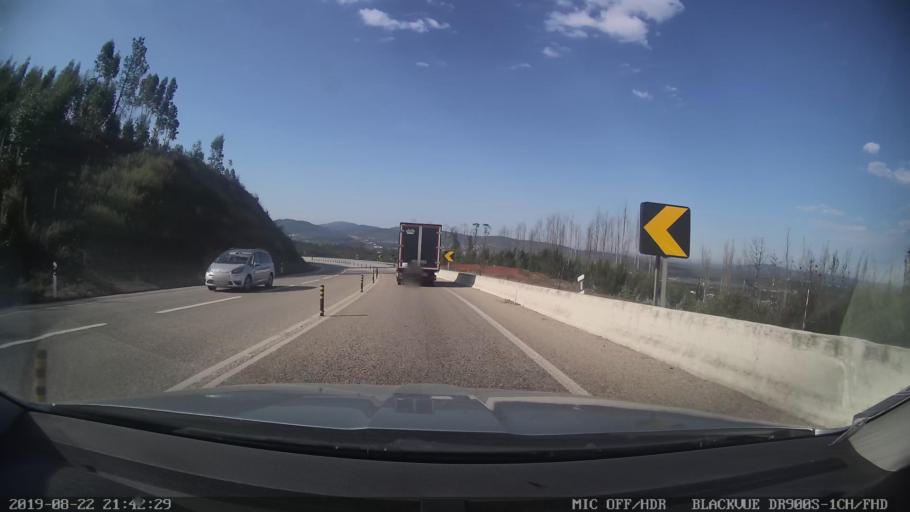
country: PT
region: Leiria
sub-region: Figueiro Dos Vinhos
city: Figueiro dos Vinhos
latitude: 39.9302
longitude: -8.3418
